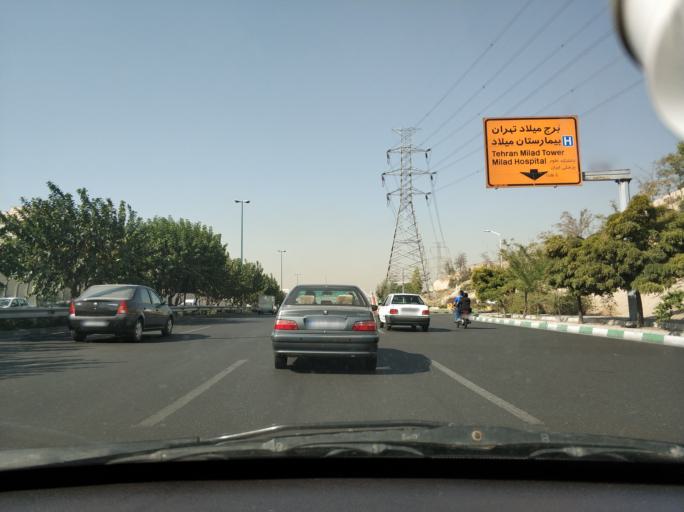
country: IR
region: Tehran
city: Tehran
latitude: 35.7419
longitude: 51.3786
